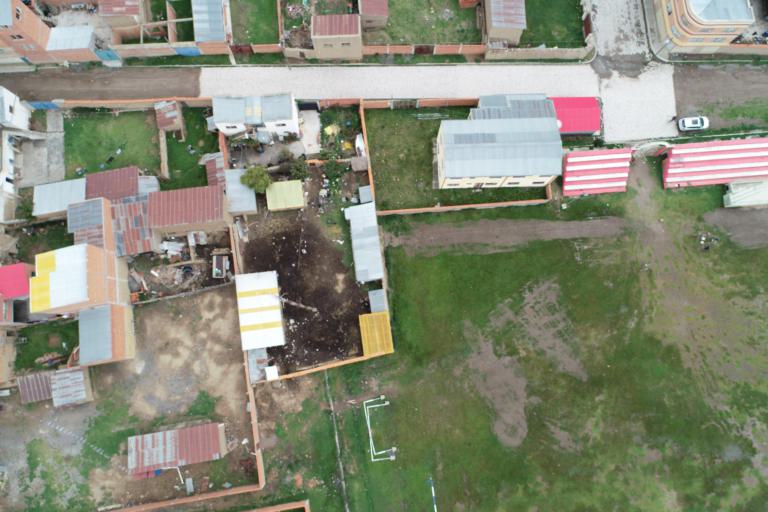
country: BO
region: La Paz
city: Huarina
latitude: -16.1915
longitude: -68.6031
